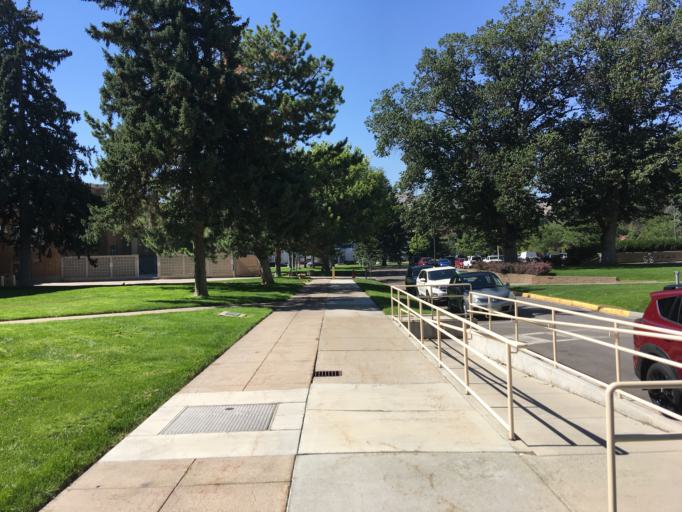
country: US
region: Idaho
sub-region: Bannock County
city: Pocatello
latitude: 42.8621
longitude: -112.4355
